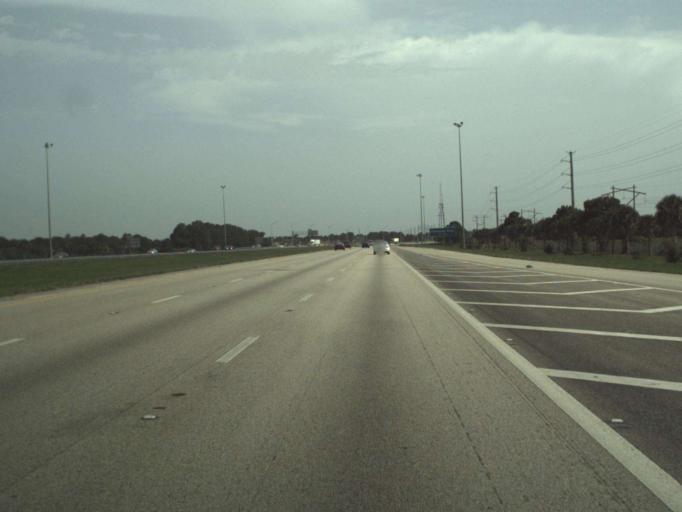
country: US
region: Florida
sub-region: Saint Lucie County
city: Port Saint Lucie
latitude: 27.3079
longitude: -80.4146
